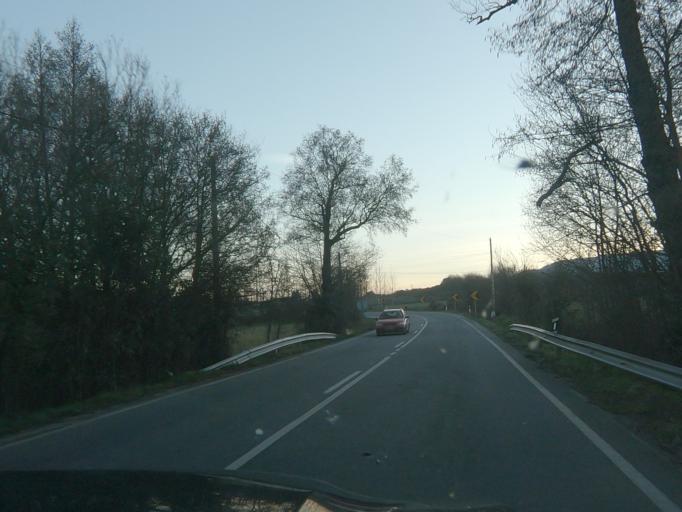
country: PT
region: Vila Real
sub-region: Vila Pouca de Aguiar
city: Vila Pouca de Aguiar
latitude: 41.4674
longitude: -7.6650
